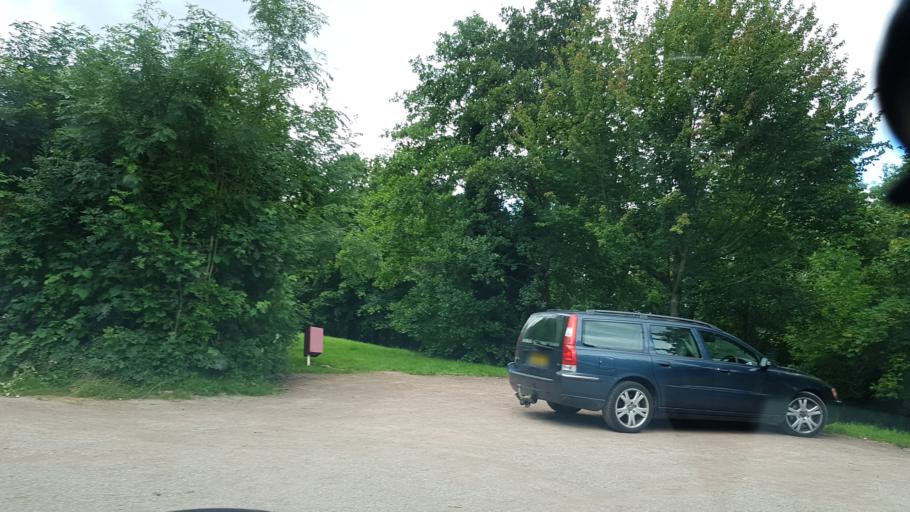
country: GB
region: Wales
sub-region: Monmouthshire
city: Gilwern
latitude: 51.8260
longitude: -3.1005
